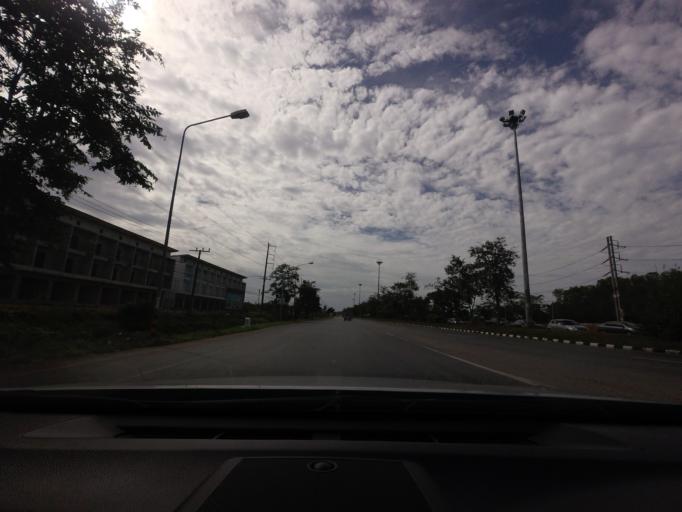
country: TH
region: Songkhla
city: Hat Yai
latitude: 7.0046
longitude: 100.4149
